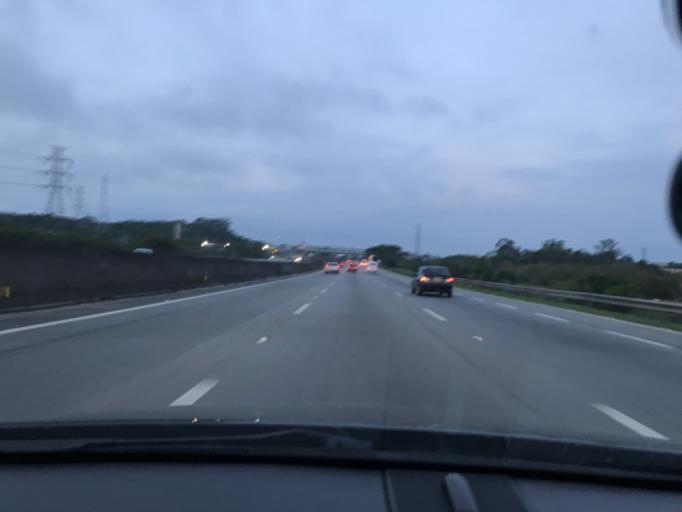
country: BR
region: Sao Paulo
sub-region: Itaquaquecetuba
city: Itaquaquecetuba
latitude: -23.4552
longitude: -46.3369
